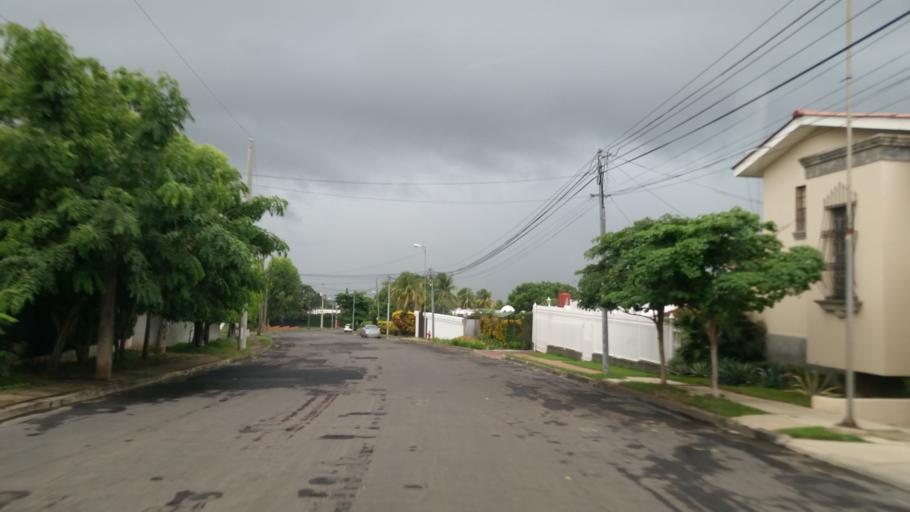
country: NI
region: Managua
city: Managua
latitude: 12.0805
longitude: -86.2465
